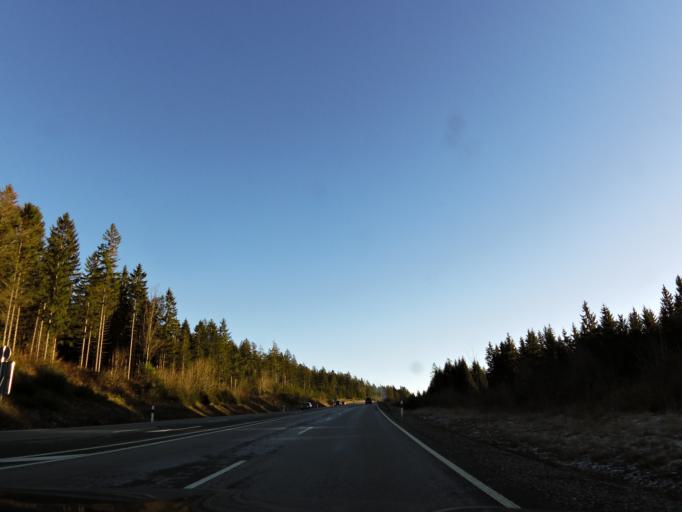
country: DE
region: Bavaria
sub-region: Upper Franconia
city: Bischofsgrun
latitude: 50.0521
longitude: 11.8277
